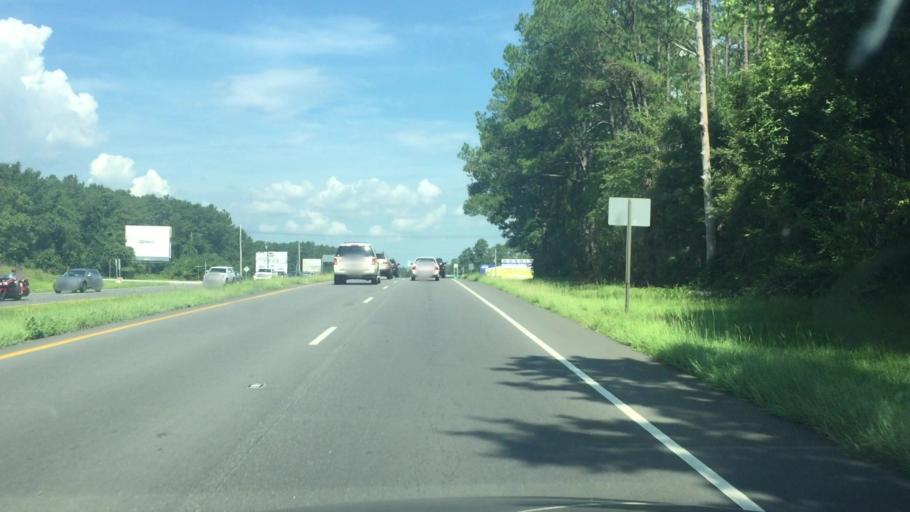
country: US
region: North Carolina
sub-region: Scotland County
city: Laurel Hill
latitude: 34.8012
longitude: -79.5362
